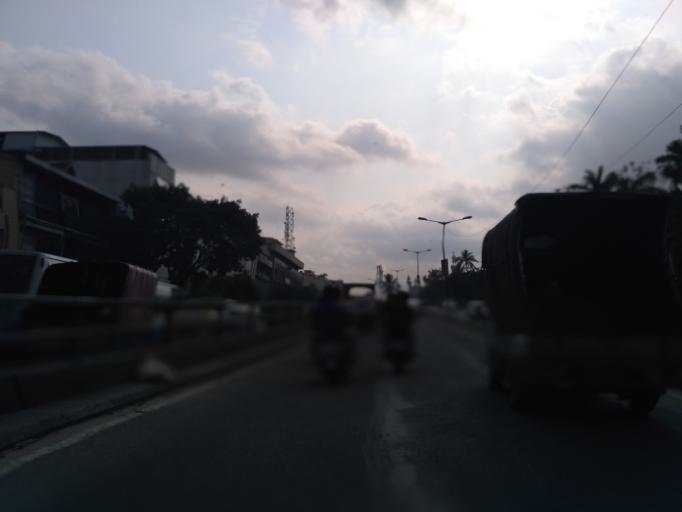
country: IN
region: Karnataka
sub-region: Bangalore Urban
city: Bangalore
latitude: 12.9635
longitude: 77.5807
